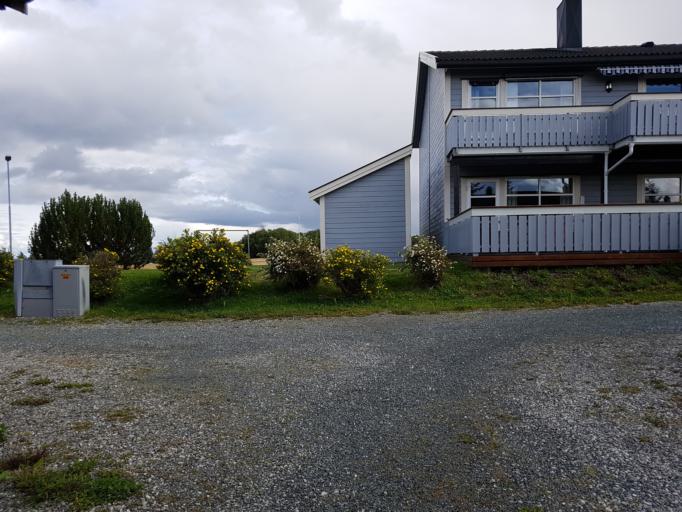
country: NO
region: Sor-Trondelag
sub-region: Trondheim
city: Trondheim
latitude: 63.4210
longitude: 10.4822
